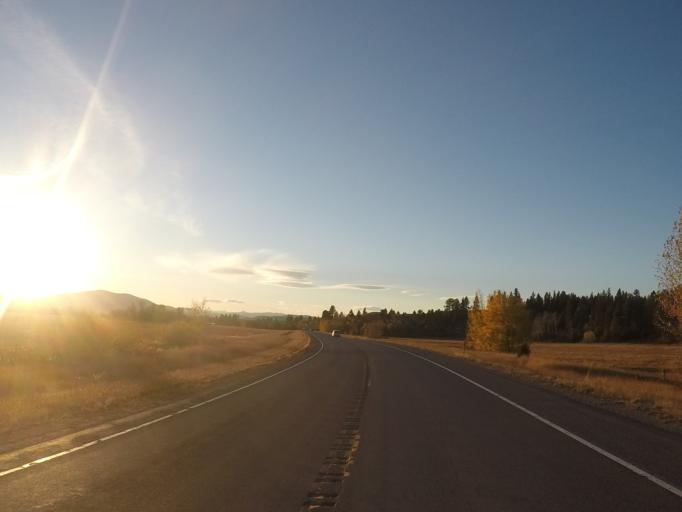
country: US
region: Montana
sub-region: Lewis and Clark County
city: Lincoln
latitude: 47.0160
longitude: -113.0723
